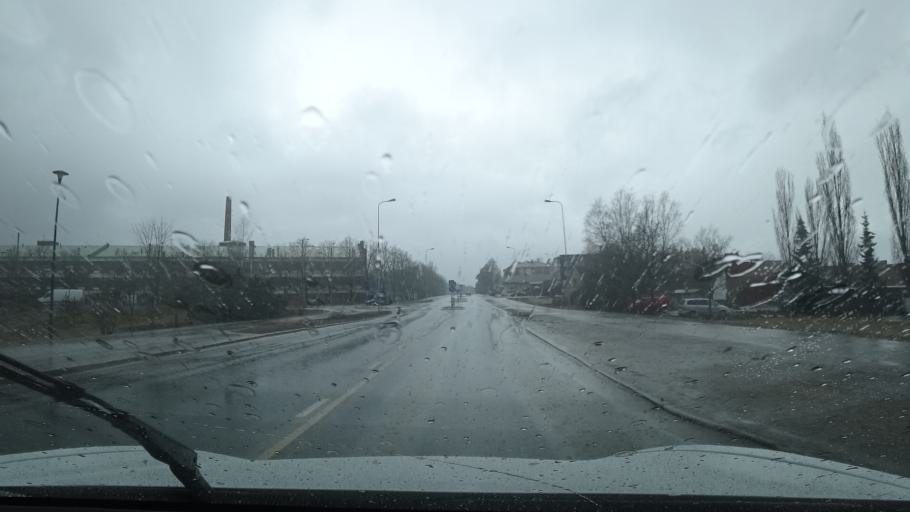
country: FI
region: Paijanne Tavastia
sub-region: Lahti
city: Orimattila
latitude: 60.8020
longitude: 25.7377
